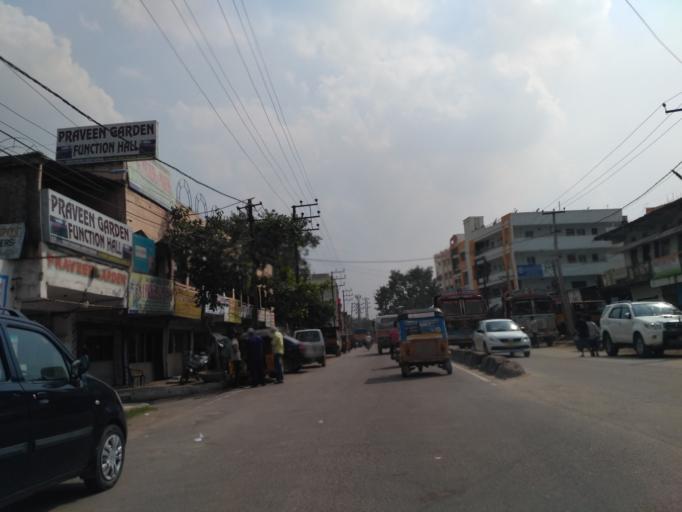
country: IN
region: Telangana
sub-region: Rangareddi
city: Kukatpalli
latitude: 17.4681
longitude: 78.4265
